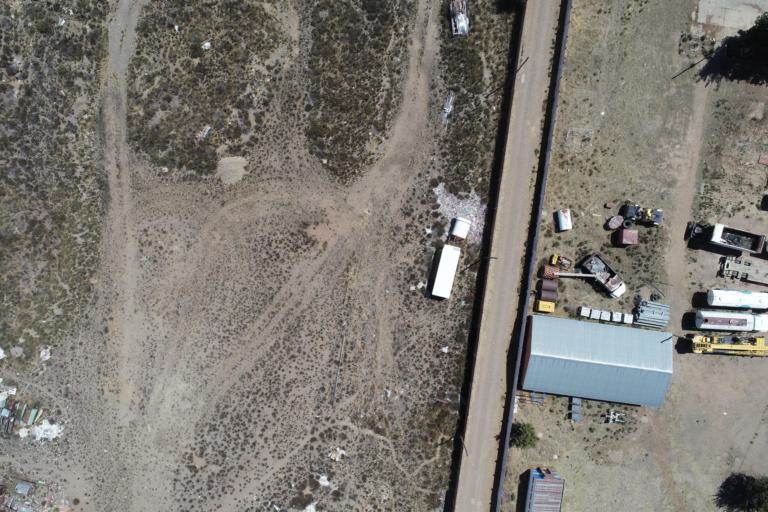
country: BO
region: La Paz
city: La Paz
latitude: -16.5690
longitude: -68.1915
